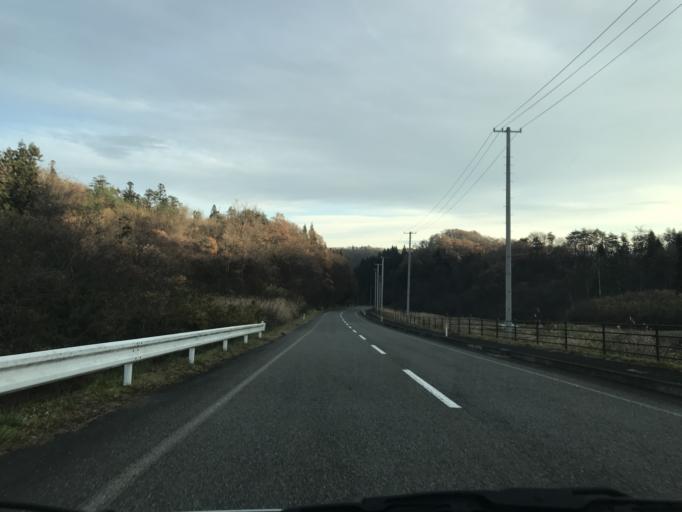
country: JP
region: Iwate
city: Ichinoseki
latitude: 38.9765
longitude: 141.0719
